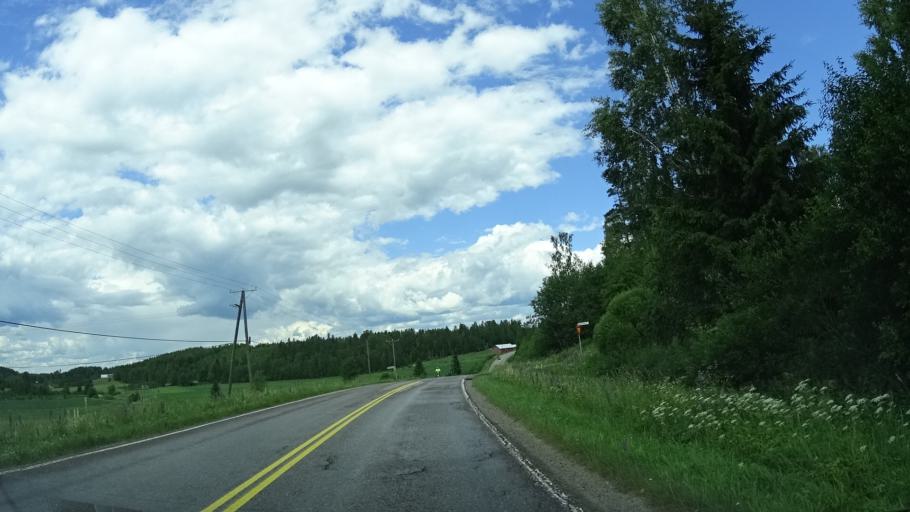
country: FI
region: Uusimaa
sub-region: Helsinki
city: Espoo
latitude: 60.3607
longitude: 24.6388
